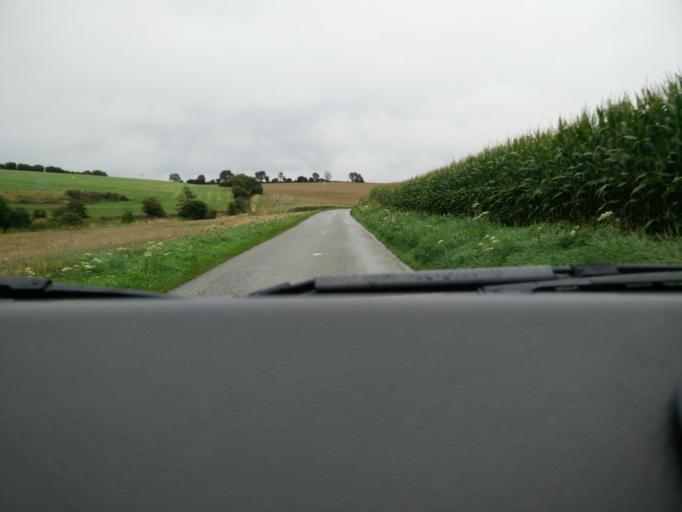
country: FR
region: Nord-Pas-de-Calais
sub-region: Departement du Pas-de-Calais
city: Campagne-les-Hesdin
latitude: 50.3372
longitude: 1.8903
